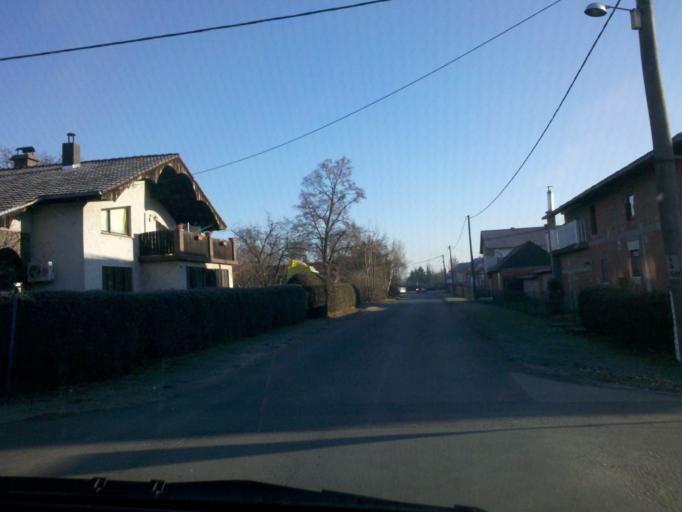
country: HR
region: Medimurska
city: Belica
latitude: 46.3999
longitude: 16.5098
